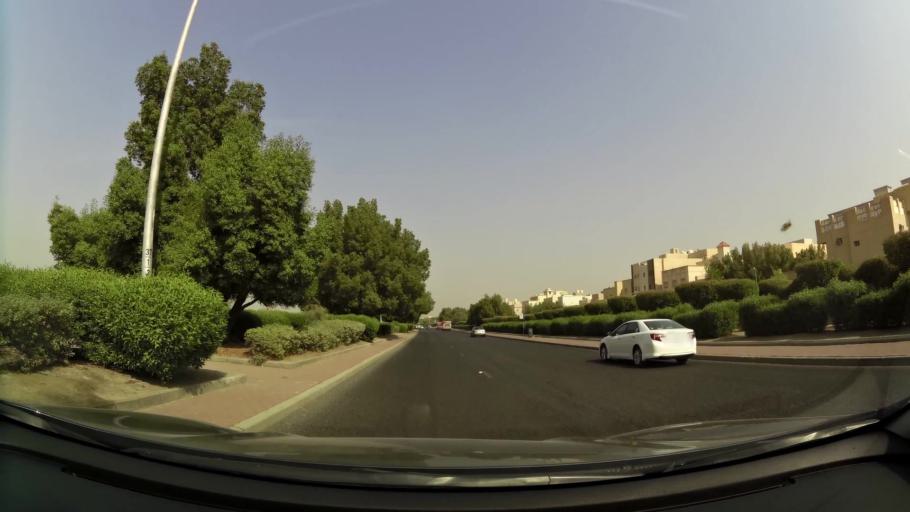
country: KW
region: Al Asimah
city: Ar Rabiyah
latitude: 29.2856
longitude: 47.9281
